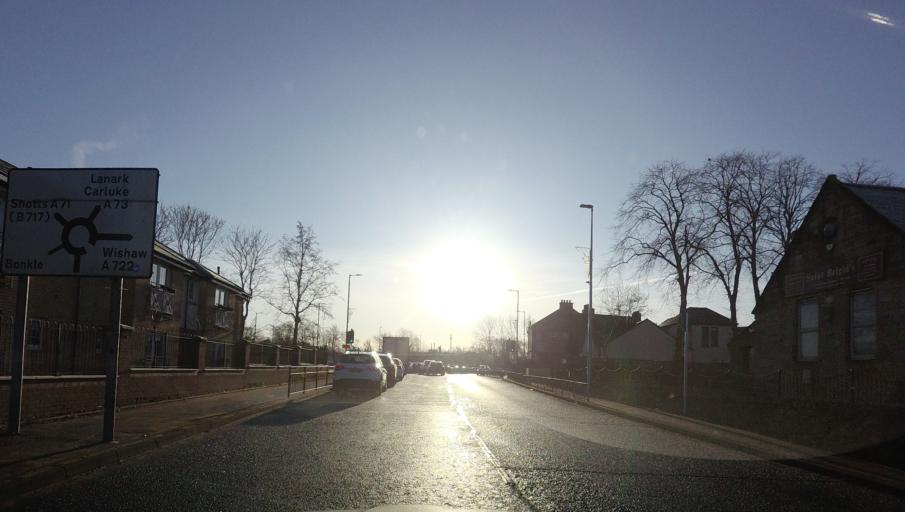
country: GB
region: Scotland
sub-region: North Lanarkshire
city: Newmains
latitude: 55.7841
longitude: -3.8774
